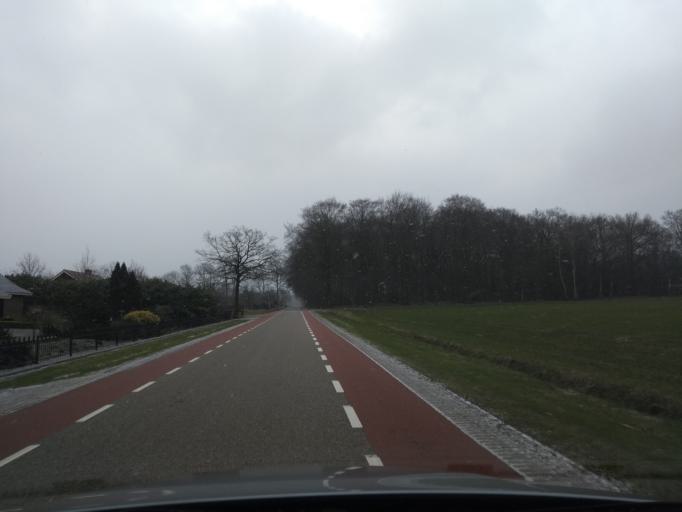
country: NL
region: Overijssel
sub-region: Gemeente Hof van Twente
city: Delden
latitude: 52.2251
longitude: 6.6963
